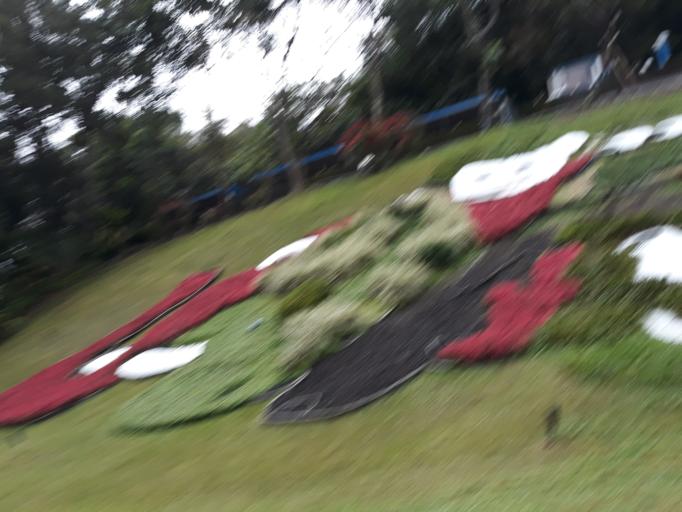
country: TW
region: Taipei
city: Taipei
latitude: 24.9957
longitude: 121.5840
